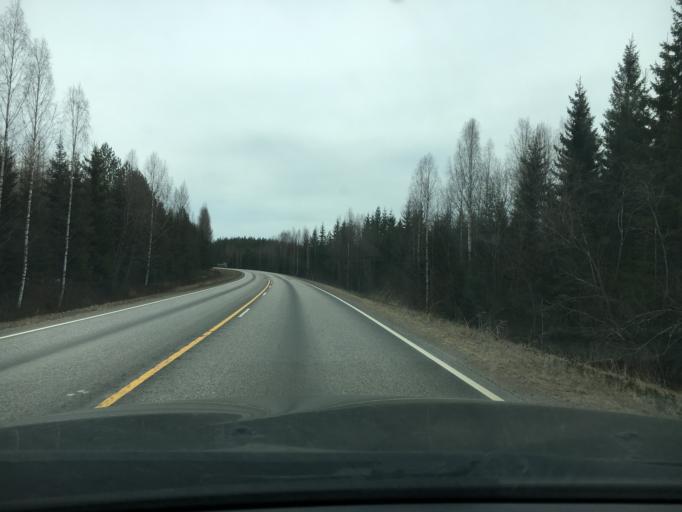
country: FI
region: Central Finland
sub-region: AEaenekoski
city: Sumiainen
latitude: 62.5826
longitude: 26.1692
